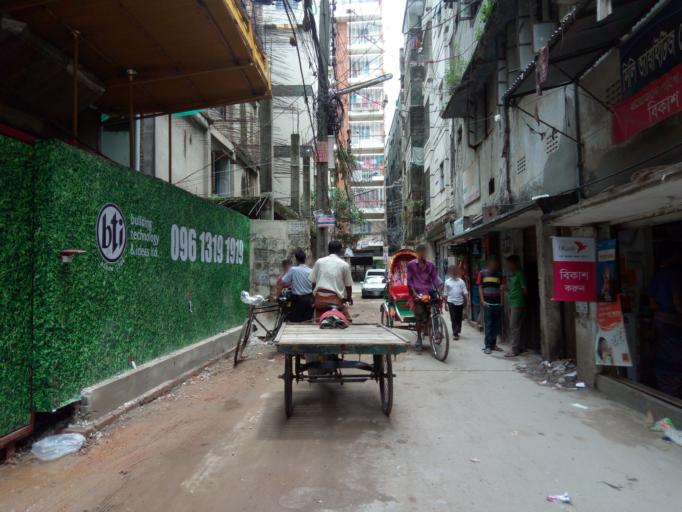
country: BD
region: Dhaka
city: Azimpur
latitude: 23.7492
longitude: 90.3843
